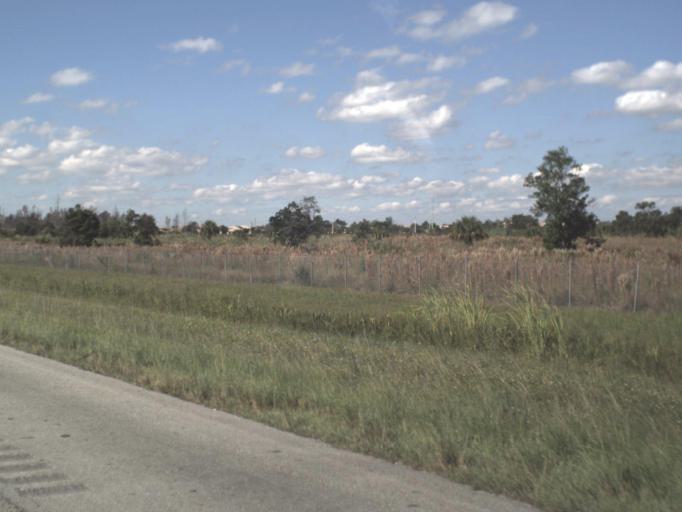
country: US
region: Florida
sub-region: Miami-Dade County
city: Country Club
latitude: 25.9617
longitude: -80.3358
